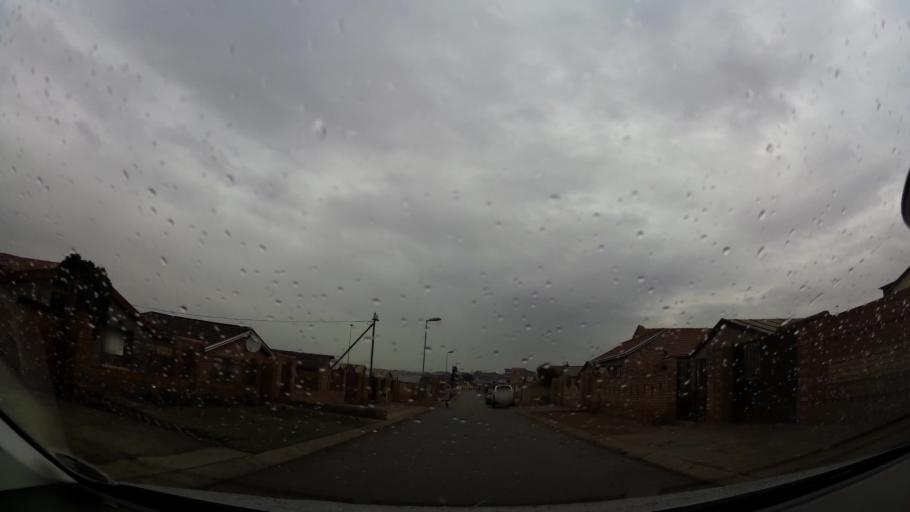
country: ZA
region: Gauteng
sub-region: City of Johannesburg Metropolitan Municipality
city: Soweto
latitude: -26.2492
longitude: 27.8694
